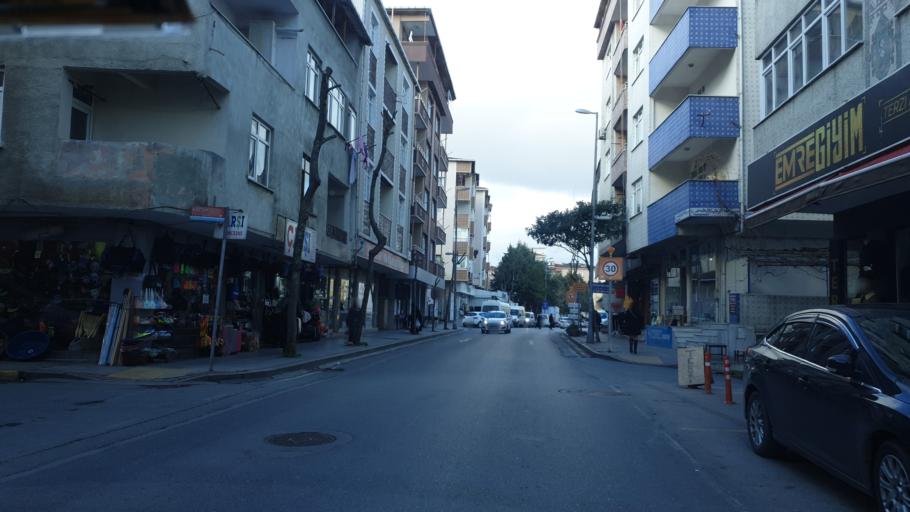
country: TR
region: Istanbul
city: Pendik
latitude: 40.8769
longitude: 29.2735
